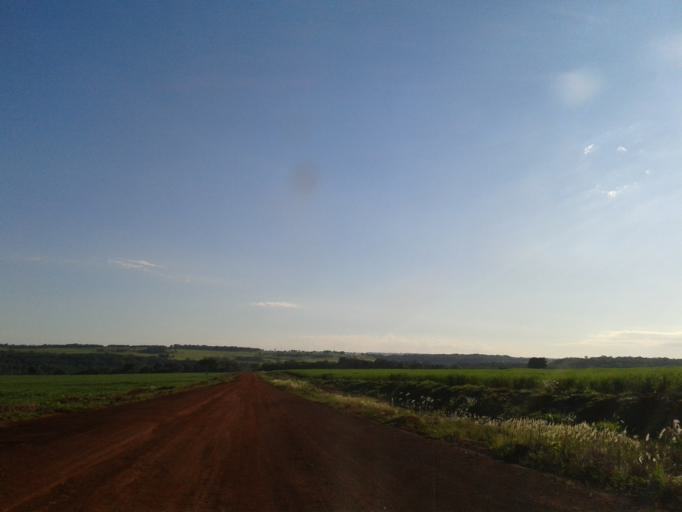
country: BR
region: Minas Gerais
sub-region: Centralina
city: Centralina
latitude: -18.7041
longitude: -49.2862
